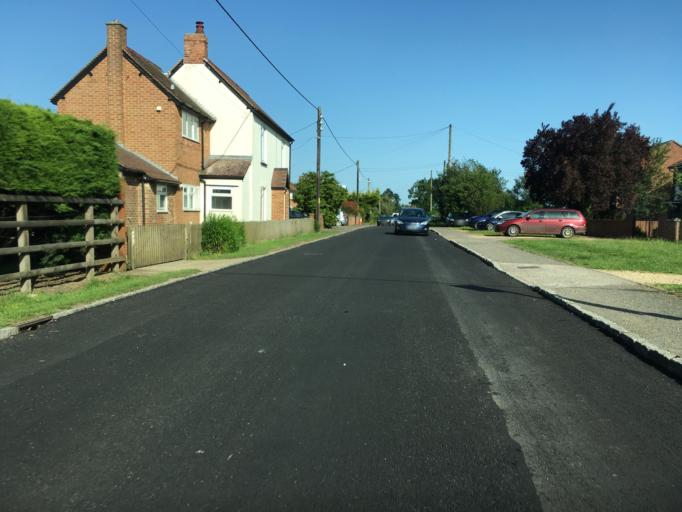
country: GB
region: England
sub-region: Buckinghamshire
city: Steeple Claydon
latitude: 51.9299
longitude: -1.0321
